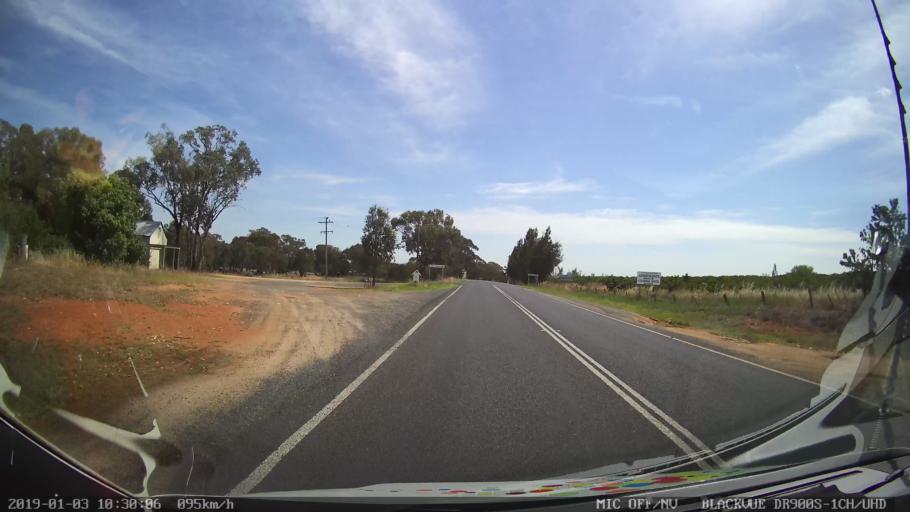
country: AU
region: New South Wales
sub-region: Young
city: Young
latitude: -34.3657
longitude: 148.2645
